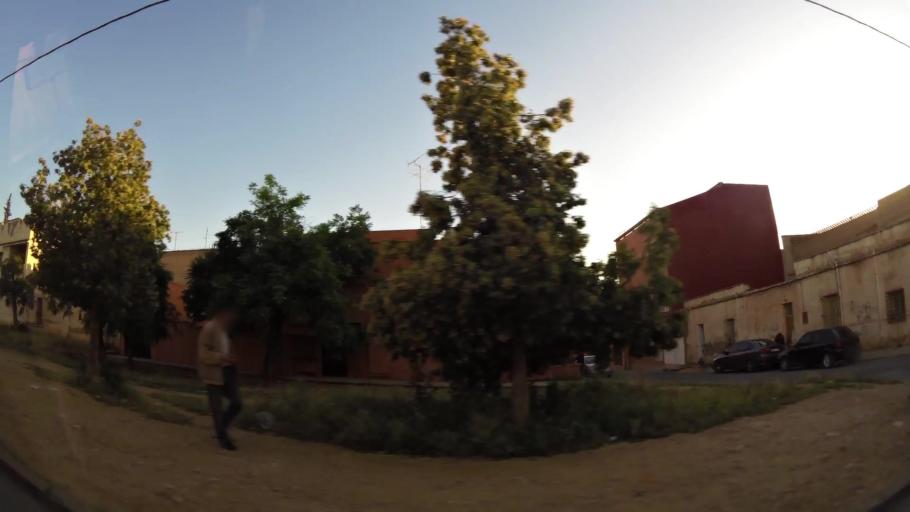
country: MA
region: Oriental
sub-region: Berkane-Taourirt
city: Berkane
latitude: 34.9252
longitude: -2.3274
